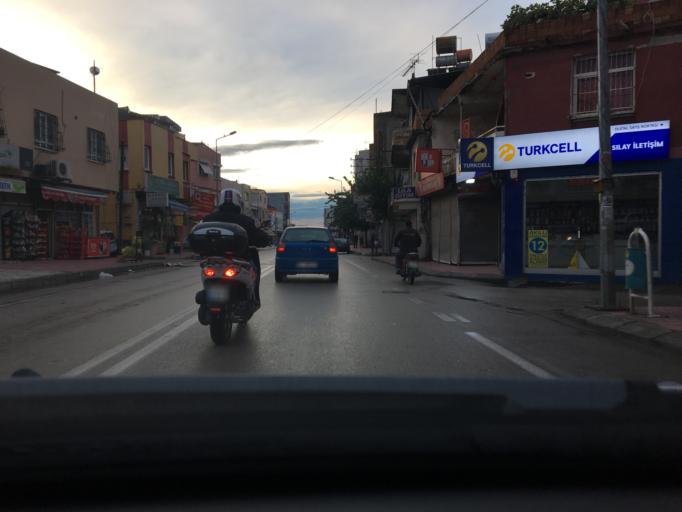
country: TR
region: Adana
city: Seyhan
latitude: 37.0177
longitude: 35.2989
